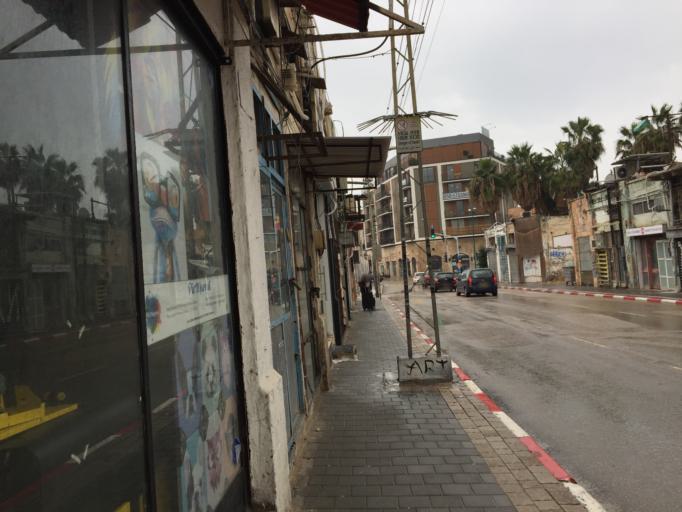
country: IL
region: Tel Aviv
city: Yafo
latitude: 32.0570
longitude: 34.7608
